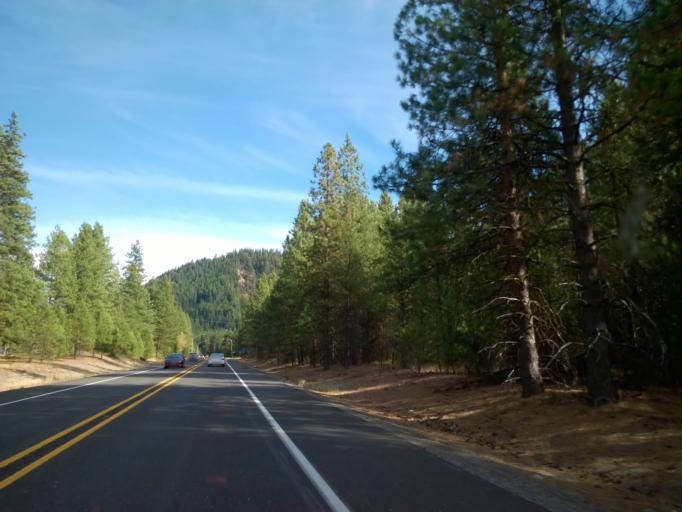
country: US
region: Washington
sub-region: Chelan County
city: Leavenworth
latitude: 47.7665
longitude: -120.7954
